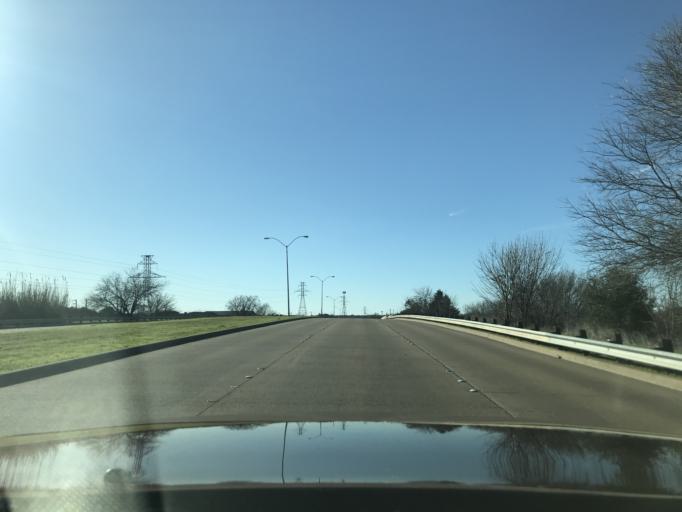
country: US
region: Texas
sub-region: Tarrant County
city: Edgecliff Village
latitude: 32.6490
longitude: -97.3520
